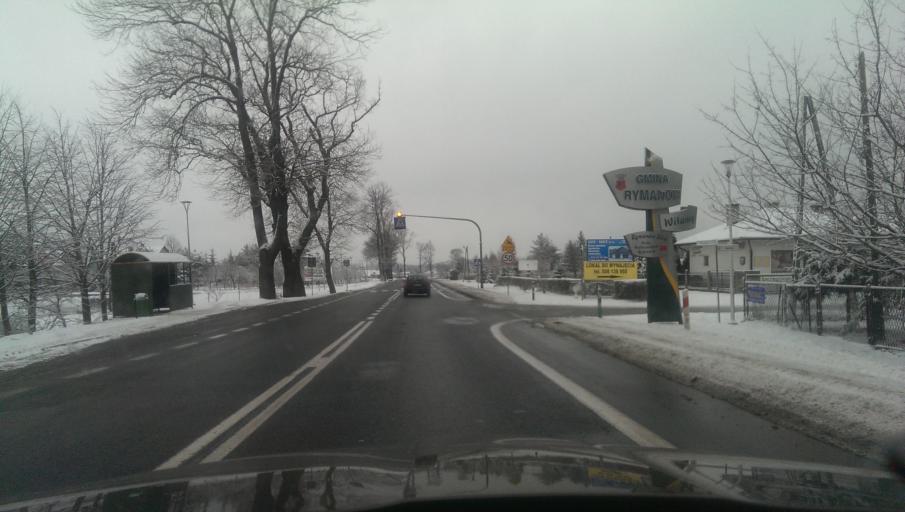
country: PL
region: Subcarpathian Voivodeship
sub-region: Powiat krosnienski
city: Rymanow
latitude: 49.5884
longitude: 21.8340
